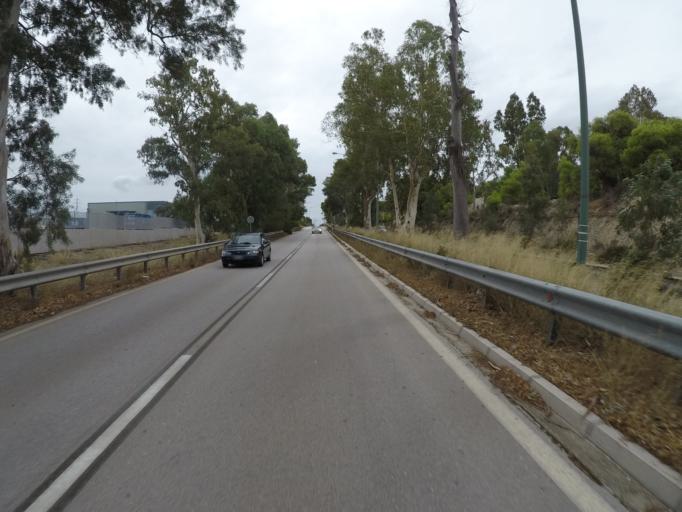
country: GR
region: Peloponnese
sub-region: Nomos Korinthias
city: Kyras Vrysi
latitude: 37.9342
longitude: 22.9889
